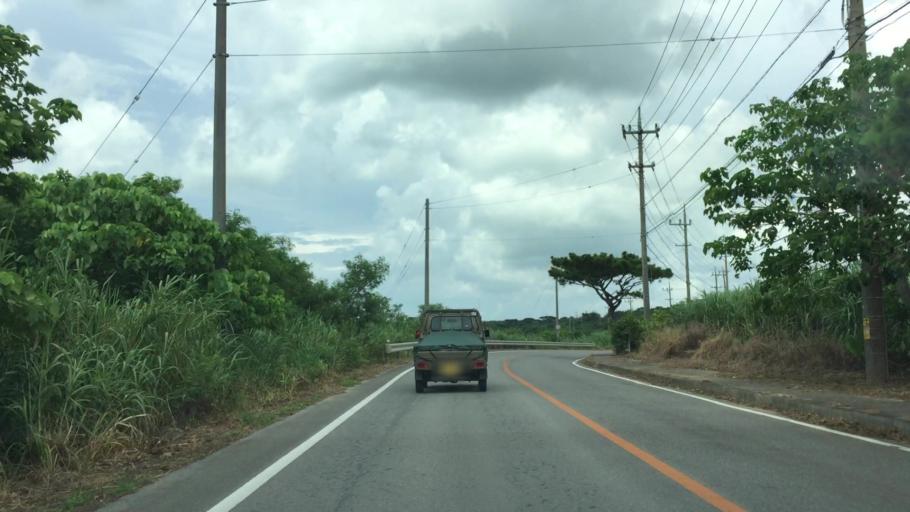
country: JP
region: Okinawa
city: Ishigaki
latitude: 24.3988
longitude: 124.1521
